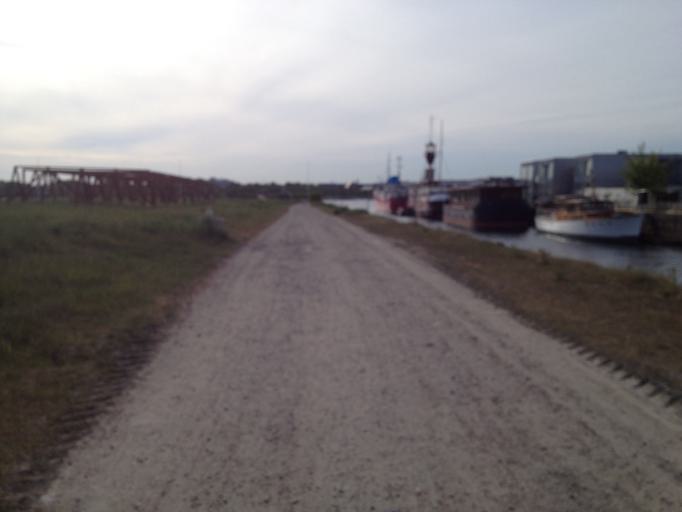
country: DK
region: Capital Region
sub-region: Kobenhavn
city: Christianshavn
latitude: 55.6918
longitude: 12.6100
